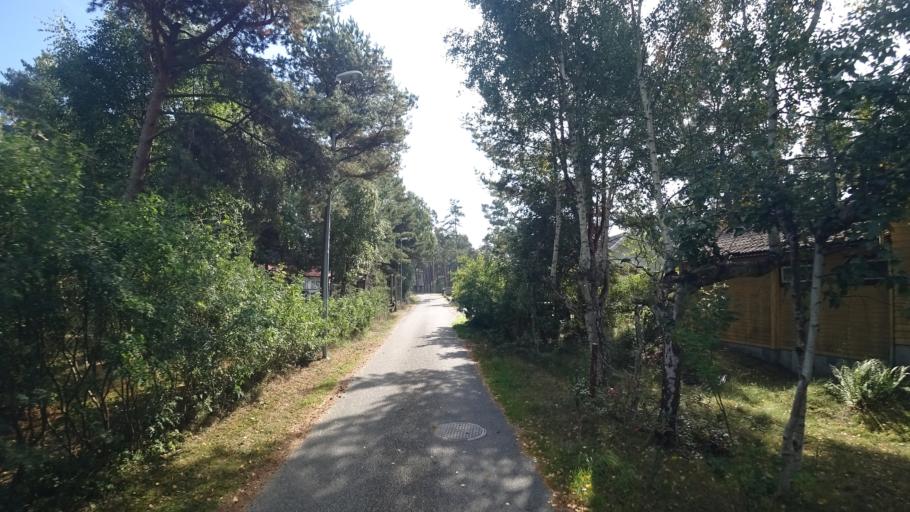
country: SE
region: Skane
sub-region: Kristianstads Kommun
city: Ahus
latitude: 55.9163
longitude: 14.3014
